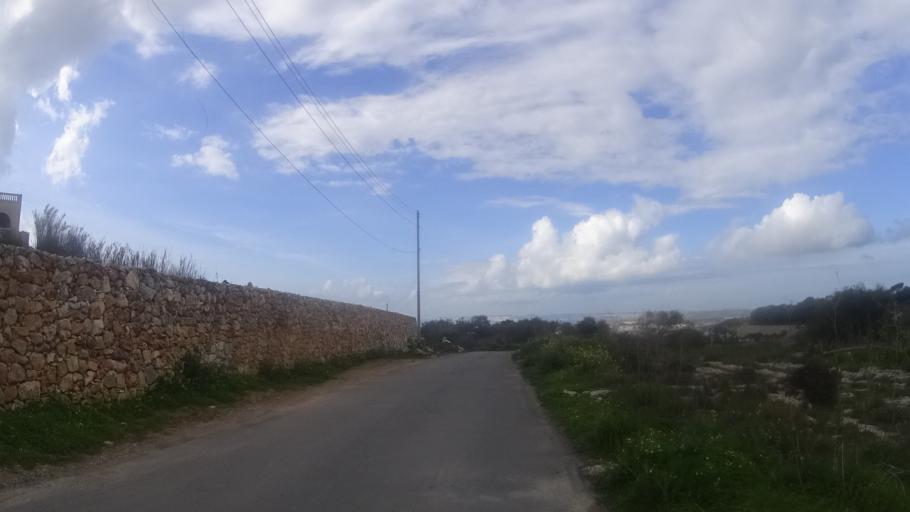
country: MT
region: L-Imtarfa
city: Imtarfa
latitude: 35.9024
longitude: 14.3789
